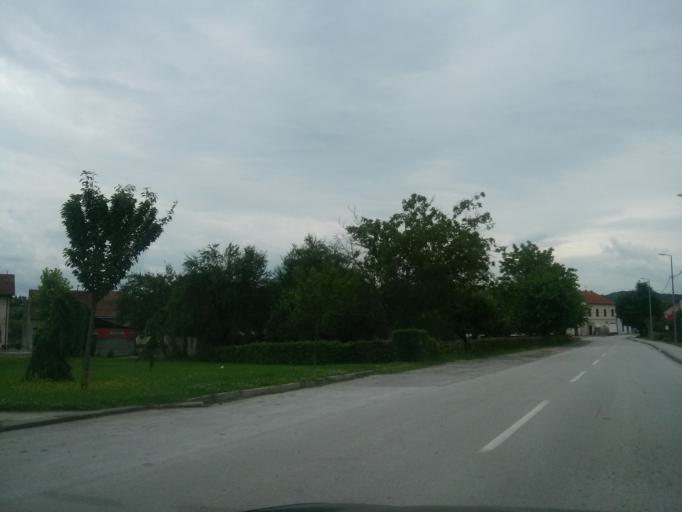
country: HR
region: Sisacko-Moslavacka
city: Gvozd
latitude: 45.2912
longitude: 15.9681
